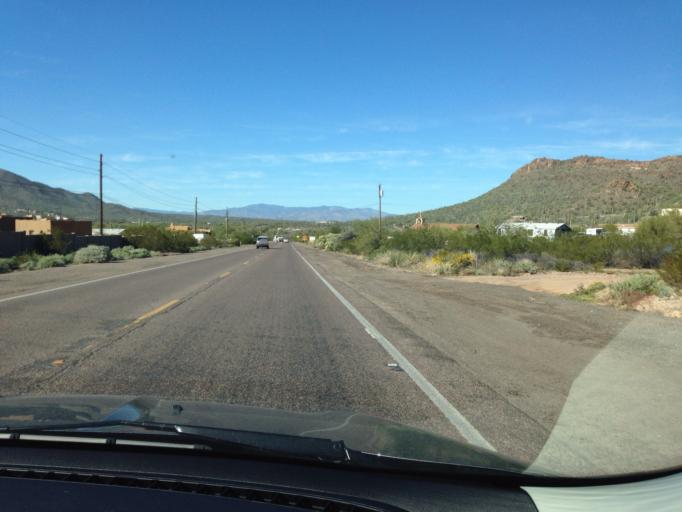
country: US
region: Arizona
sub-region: Maricopa County
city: Anthem
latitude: 33.8690
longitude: -112.0626
